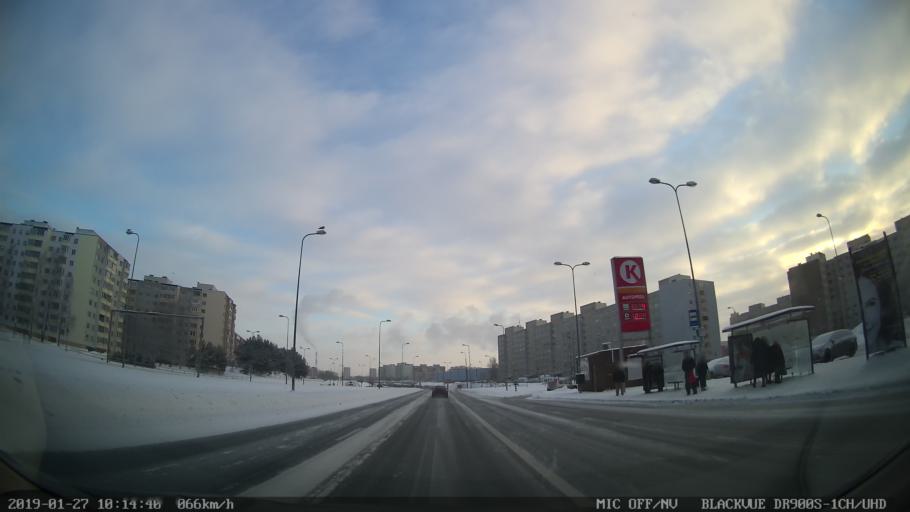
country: EE
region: Harju
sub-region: Tallinna linn
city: Kose
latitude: 59.4429
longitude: 24.8753
